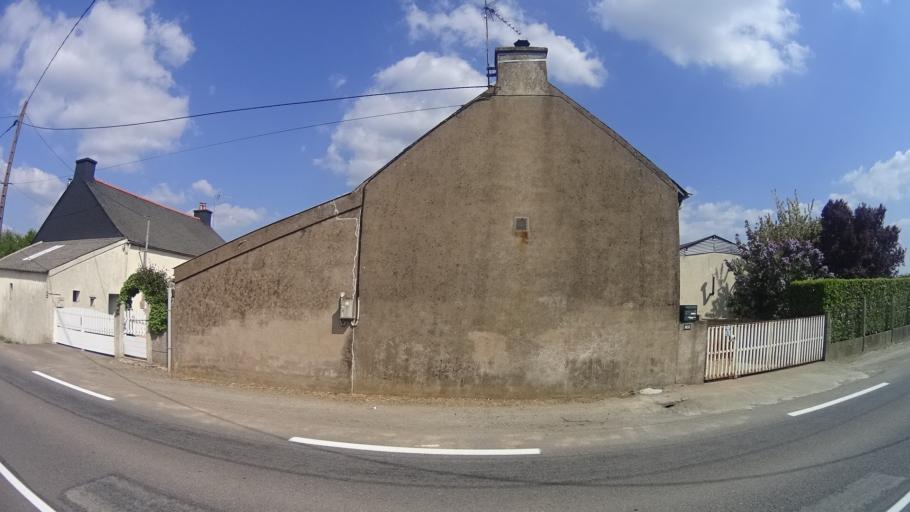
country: FR
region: Brittany
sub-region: Departement du Morbihan
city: Rieux
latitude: 47.5891
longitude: -2.1102
